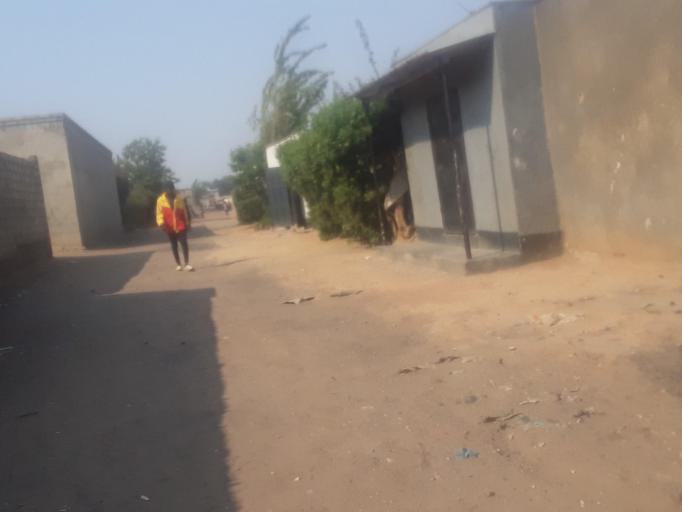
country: ZM
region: Lusaka
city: Lusaka
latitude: -15.3573
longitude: 28.2890
